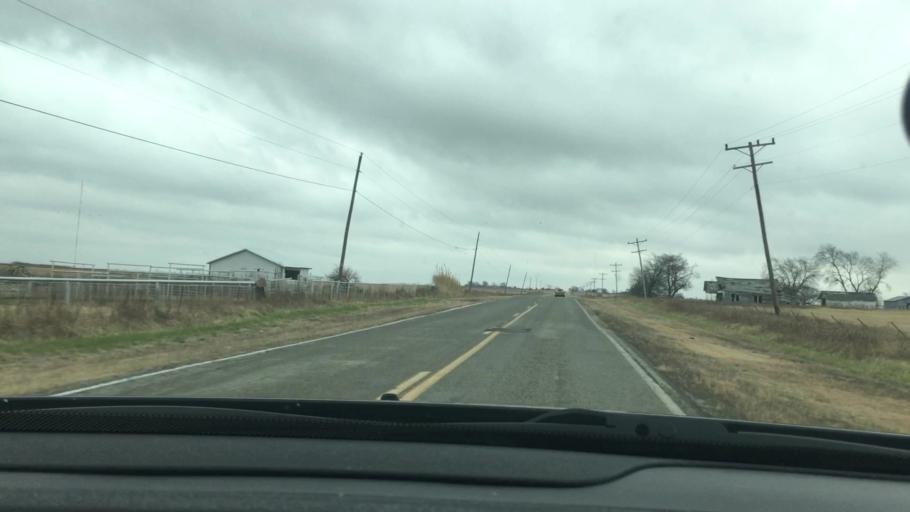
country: US
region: Oklahoma
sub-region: Johnston County
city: Tishomingo
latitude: 34.1434
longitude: -96.5213
